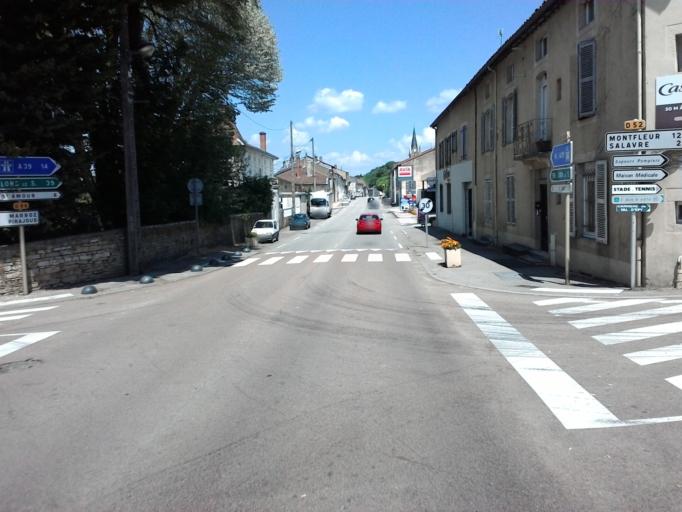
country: FR
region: Rhone-Alpes
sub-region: Departement de l'Ain
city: Coligny
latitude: 46.3806
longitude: 5.3448
